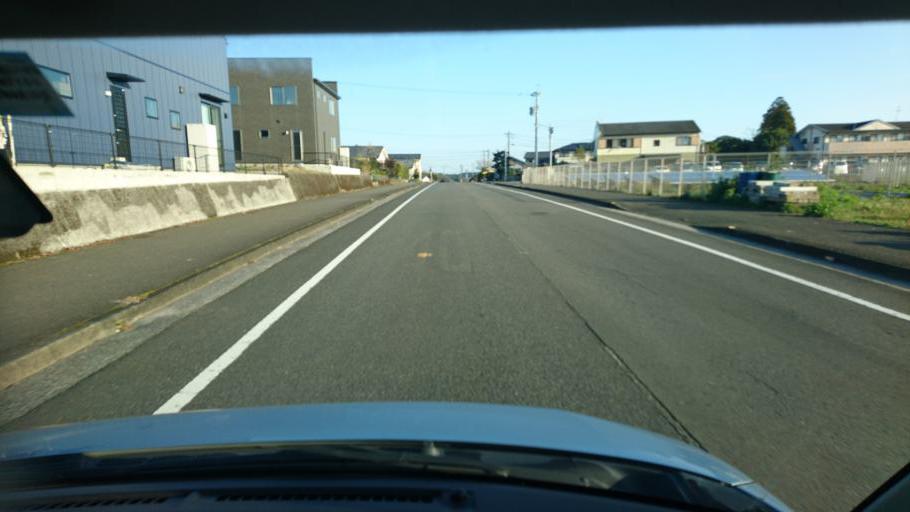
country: JP
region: Miyazaki
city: Miyazaki-shi
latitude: 31.8335
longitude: 131.4199
